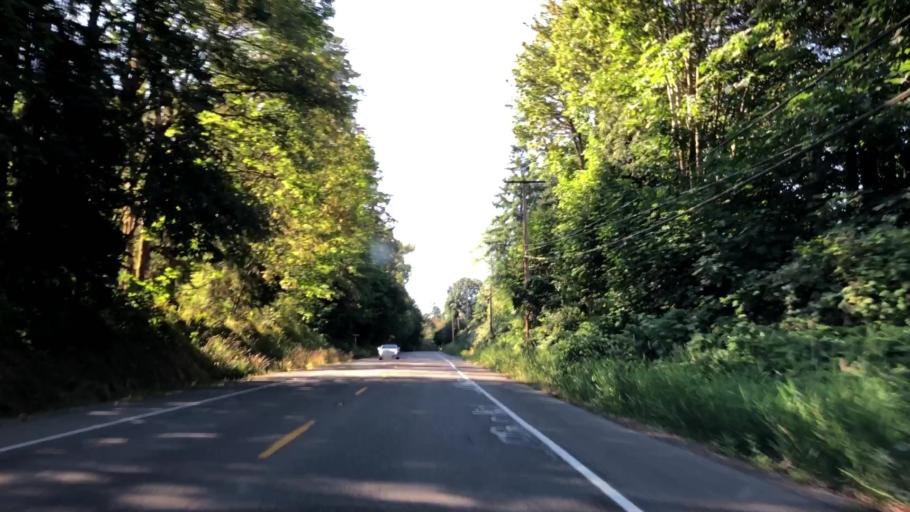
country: US
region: Washington
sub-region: Kitsap County
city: Kingston
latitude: 47.7835
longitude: -122.5016
